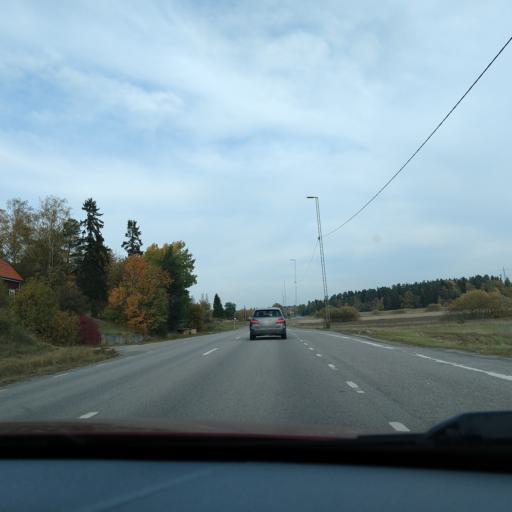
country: SE
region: Stockholm
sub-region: Upplands Vasby Kommun
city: Upplands Vaesby
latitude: 59.5314
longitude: 17.9899
